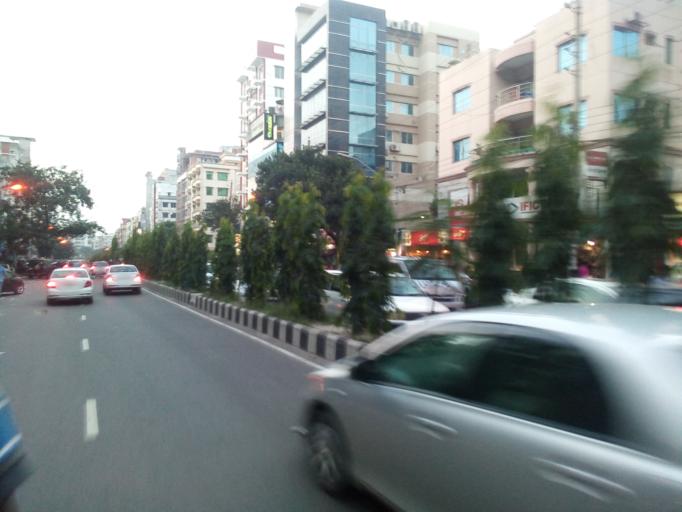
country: BD
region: Dhaka
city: Tungi
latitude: 23.8756
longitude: 90.3908
